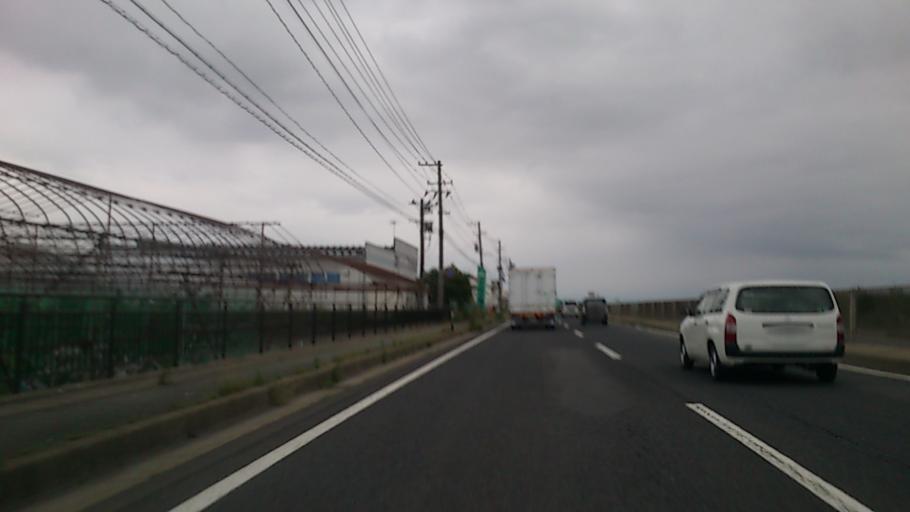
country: JP
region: Yamagata
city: Higashine
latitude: 38.4156
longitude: 140.3749
